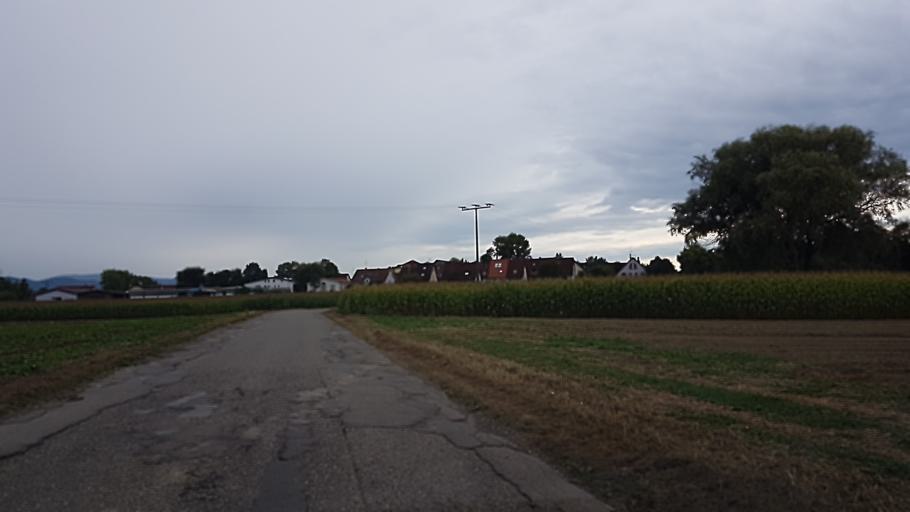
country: DE
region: Baden-Wuerttemberg
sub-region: Freiburg Region
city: Merdingen
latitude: 47.9940
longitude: 7.7185
